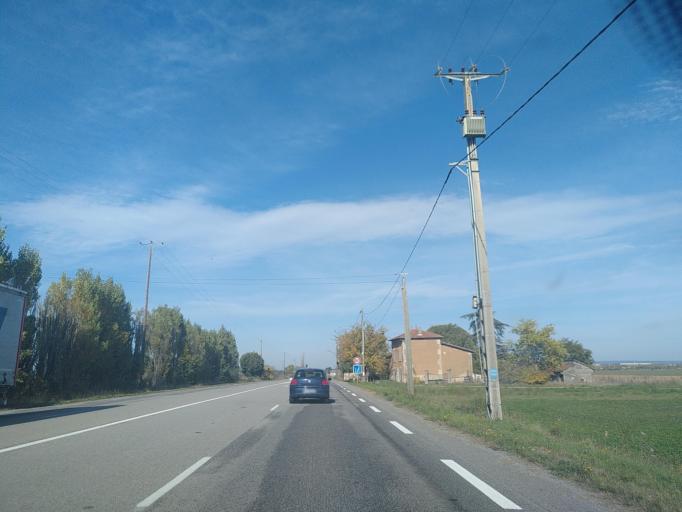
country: FR
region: Rhone-Alpes
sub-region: Departement de la Drome
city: Andancette
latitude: 45.2473
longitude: 4.8212
